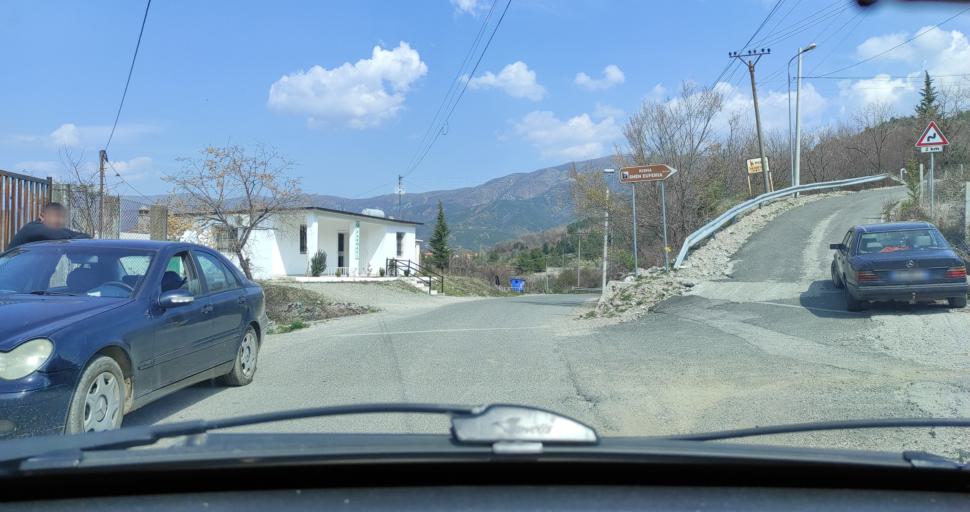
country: AL
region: Lezhe
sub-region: Rrethi i Lezhes
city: Kallmeti i Madh
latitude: 41.8507
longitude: 19.6917
